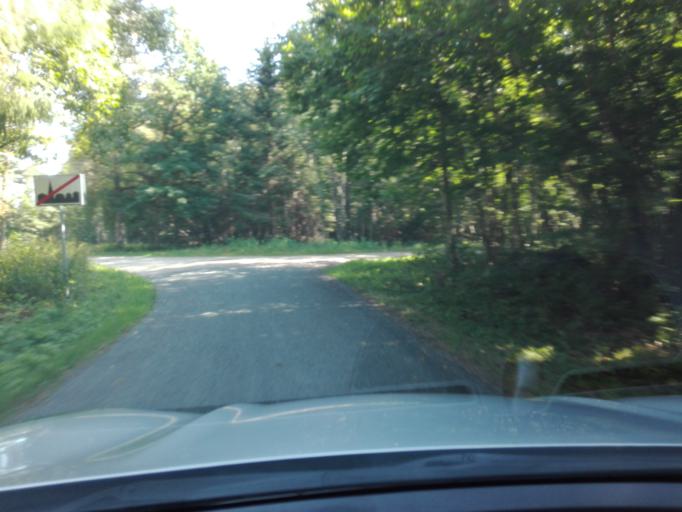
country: EE
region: Raplamaa
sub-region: Rapla vald
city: Rapla
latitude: 59.0641
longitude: 24.8114
